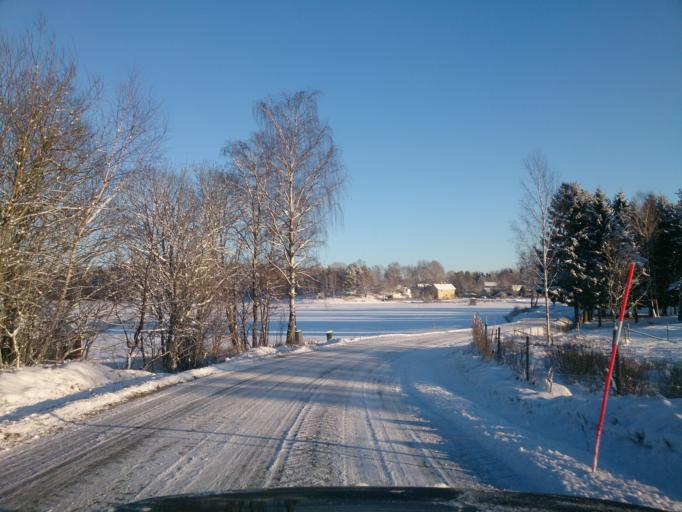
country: SE
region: OEstergoetland
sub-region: Norrkopings Kommun
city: Krokek
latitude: 58.5078
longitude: 16.5941
